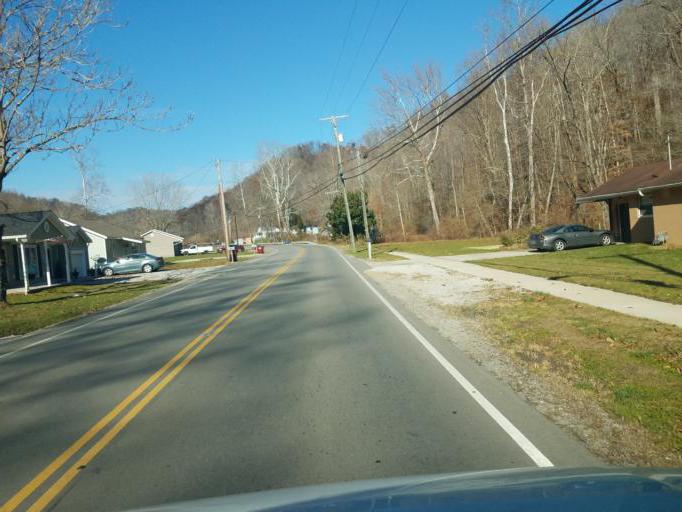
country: US
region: Ohio
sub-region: Scioto County
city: New Boston
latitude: 38.7803
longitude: -82.9456
